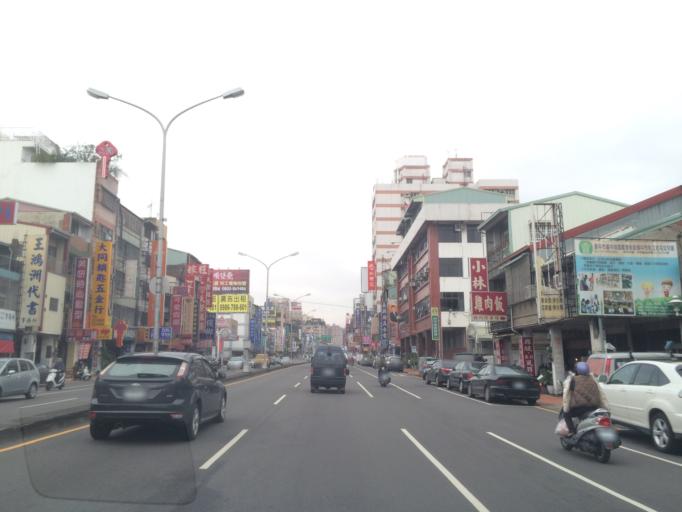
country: TW
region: Taiwan
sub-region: Taichung City
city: Taichung
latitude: 24.1634
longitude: 120.6934
